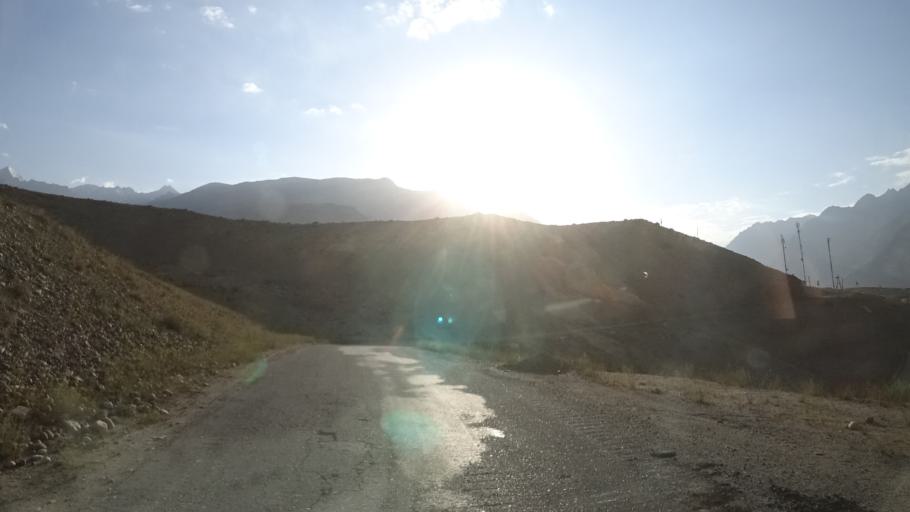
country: TJ
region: Gorno-Badakhshan
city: Vanj
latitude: 38.2912
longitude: 71.3399
